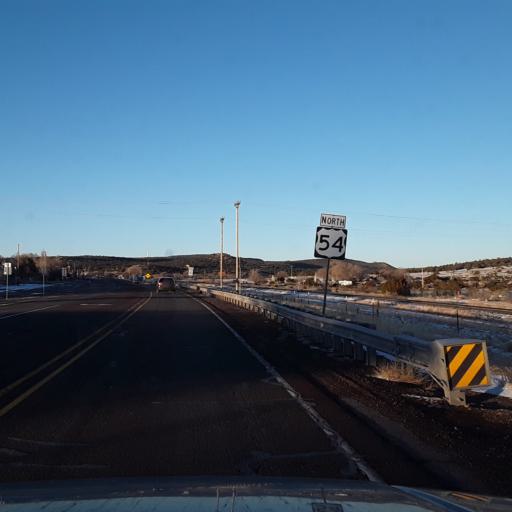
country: US
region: New Mexico
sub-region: Lincoln County
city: Carrizozo
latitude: 34.2450
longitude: -105.5952
